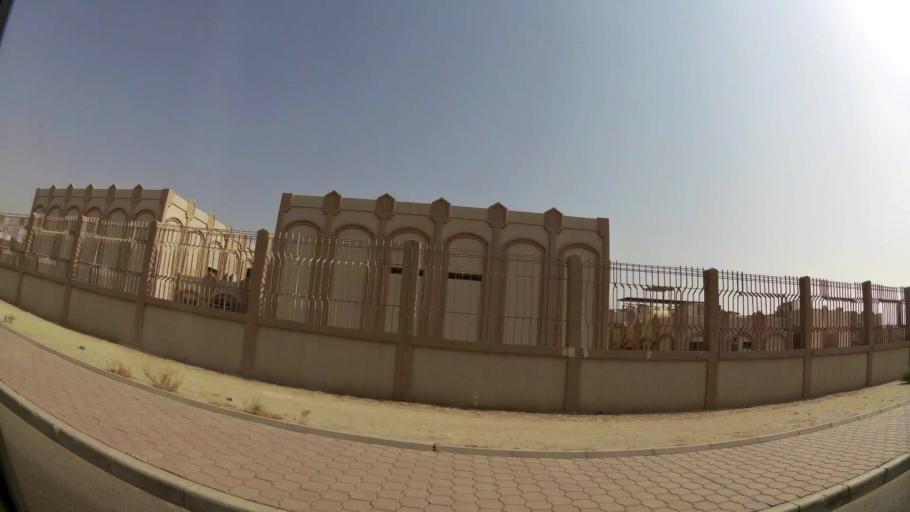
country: KW
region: Muhafazat al Jahra'
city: Al Jahra'
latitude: 29.3374
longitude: 47.7705
